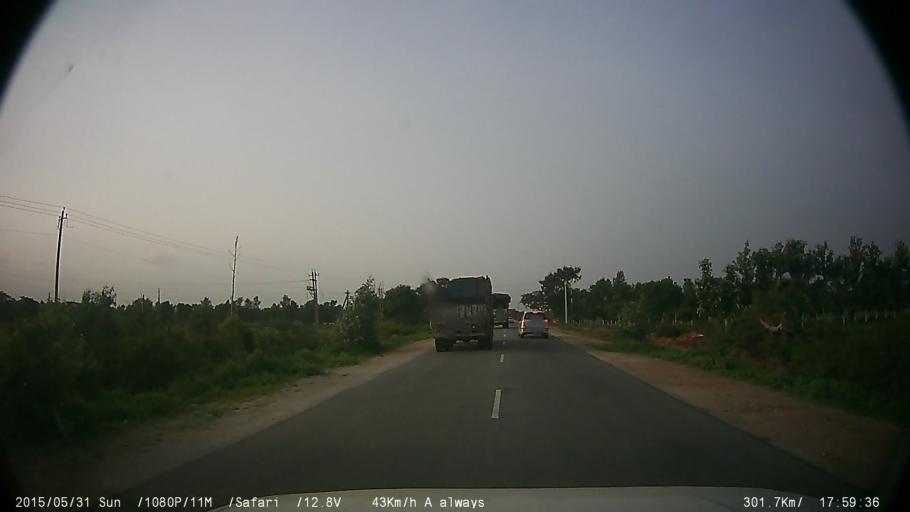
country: IN
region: Karnataka
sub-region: Mysore
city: Nanjangud
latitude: 12.0160
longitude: 76.6716
